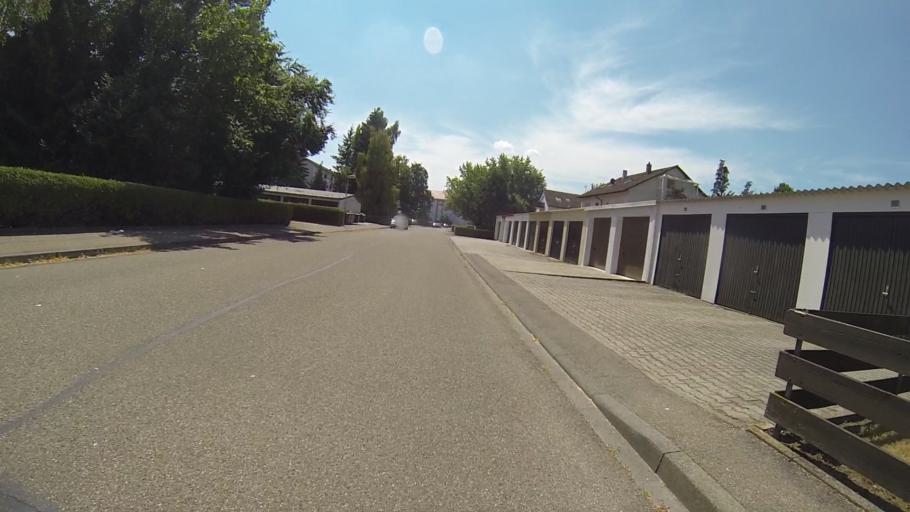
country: DE
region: Baden-Wuerttemberg
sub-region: Regierungsbezirk Stuttgart
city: Giengen an der Brenz
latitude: 48.6267
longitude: 10.2372
